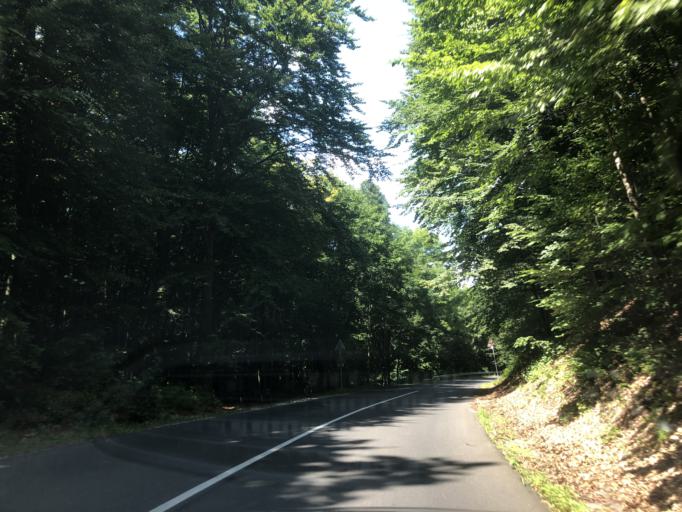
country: HU
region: Borsod-Abauj-Zemplen
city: Rudabanya
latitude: 48.4778
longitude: 20.5447
